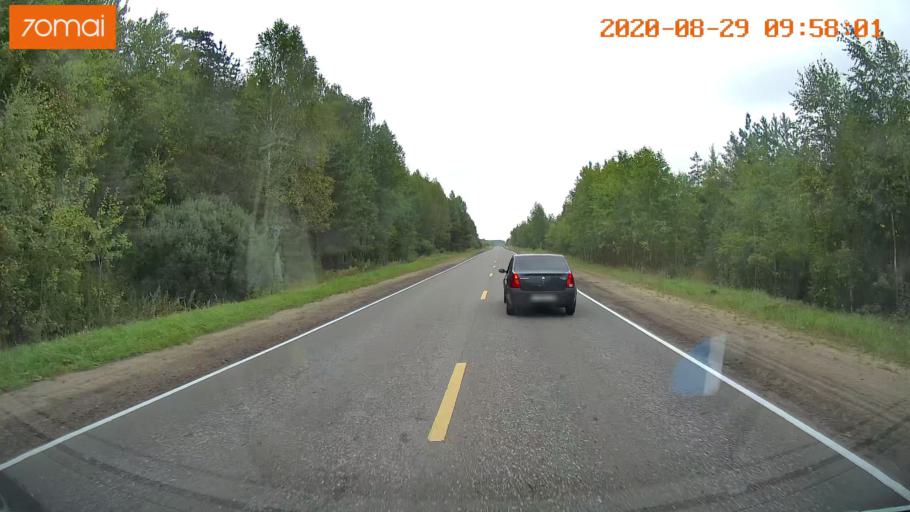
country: RU
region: Ivanovo
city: Zarechnyy
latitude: 57.4147
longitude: 42.3284
